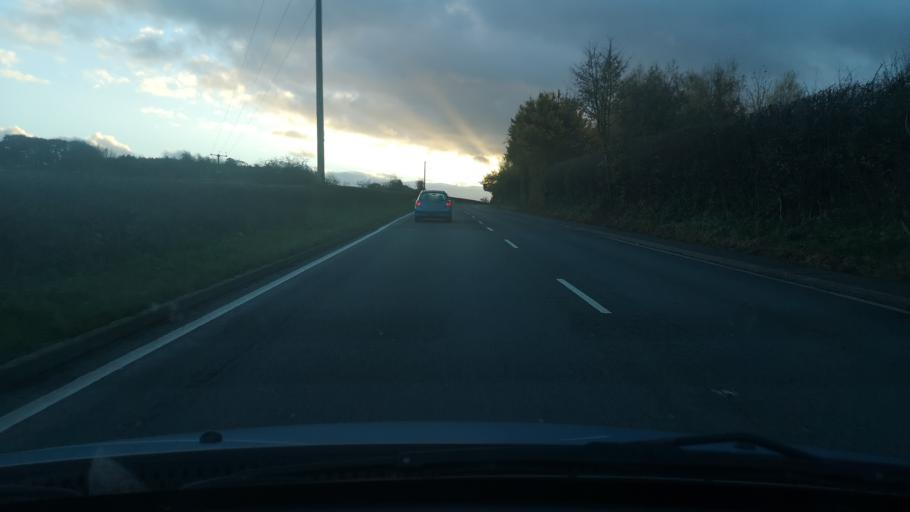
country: GB
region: England
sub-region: City and Borough of Wakefield
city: Horbury
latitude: 53.6292
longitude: -1.5677
